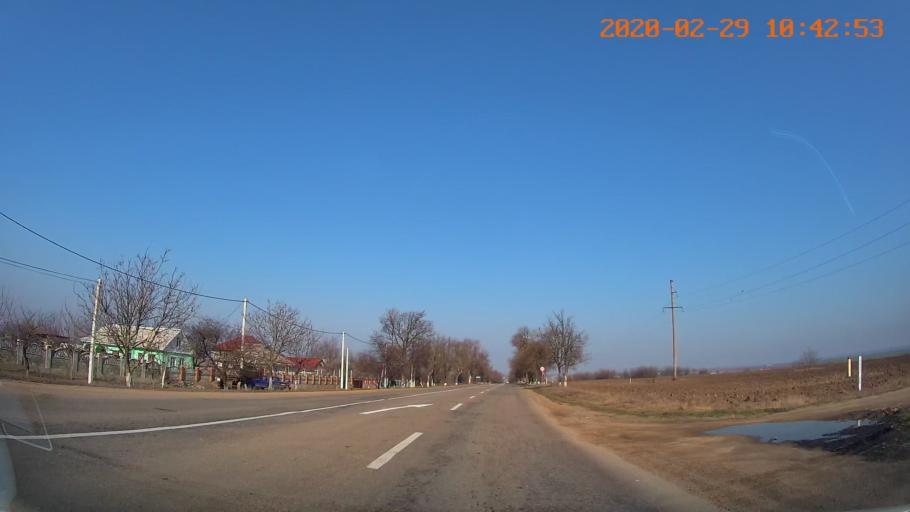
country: MD
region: Telenesti
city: Grigoriopol
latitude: 47.0551
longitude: 29.4061
